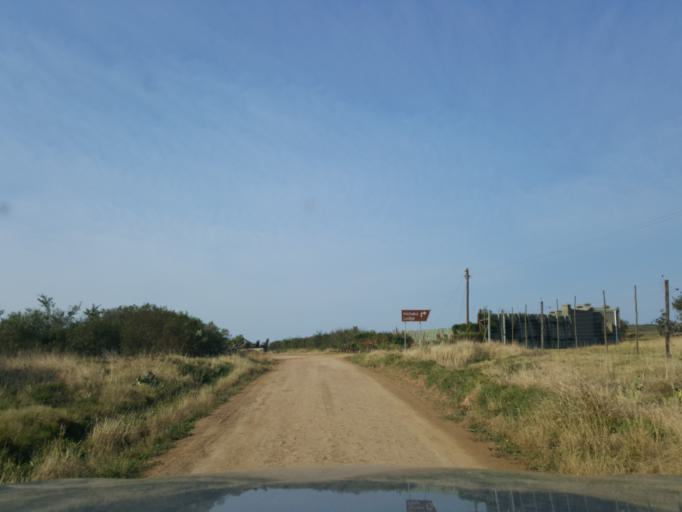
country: ZA
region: Eastern Cape
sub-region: Cacadu District Municipality
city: Grahamstown
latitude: -33.4085
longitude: 26.2994
